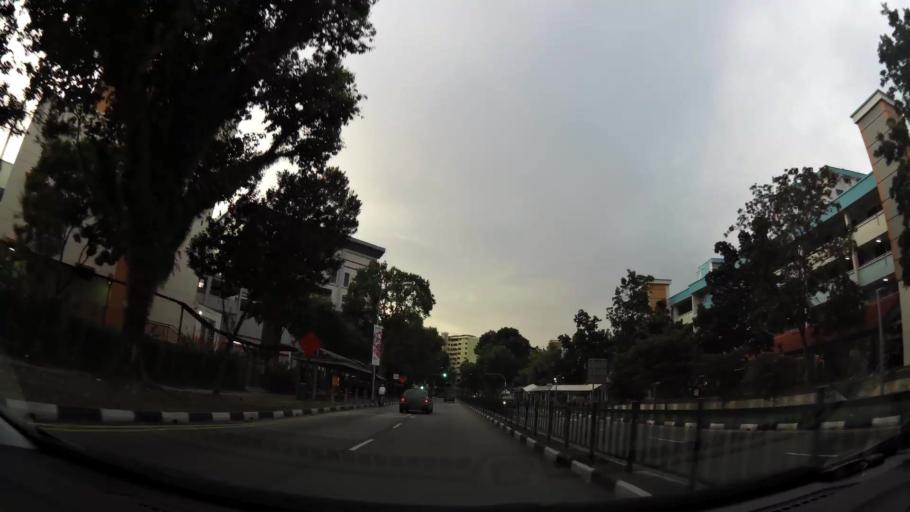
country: MY
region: Johor
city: Kampung Pasir Gudang Baru
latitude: 1.4281
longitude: 103.8310
